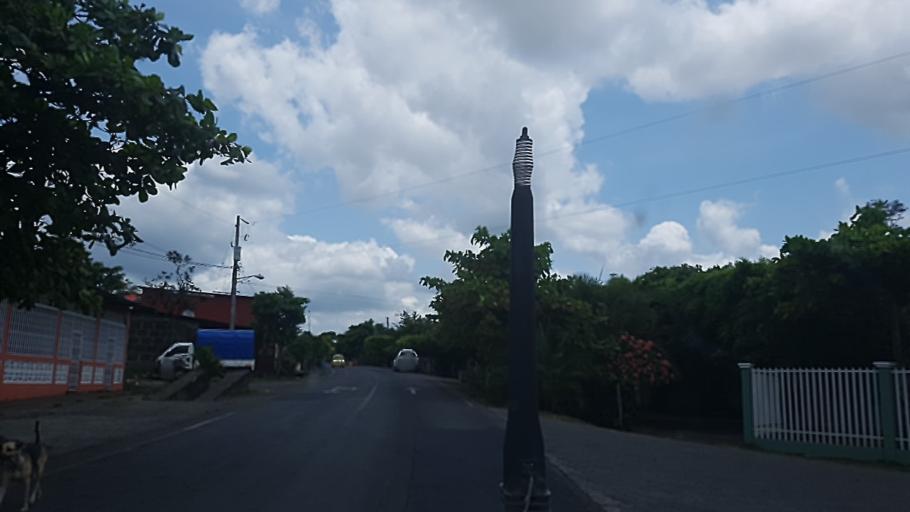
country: NI
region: Atlantico Sur
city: Muelle de los Bueyes
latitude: 11.9158
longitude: -84.6451
